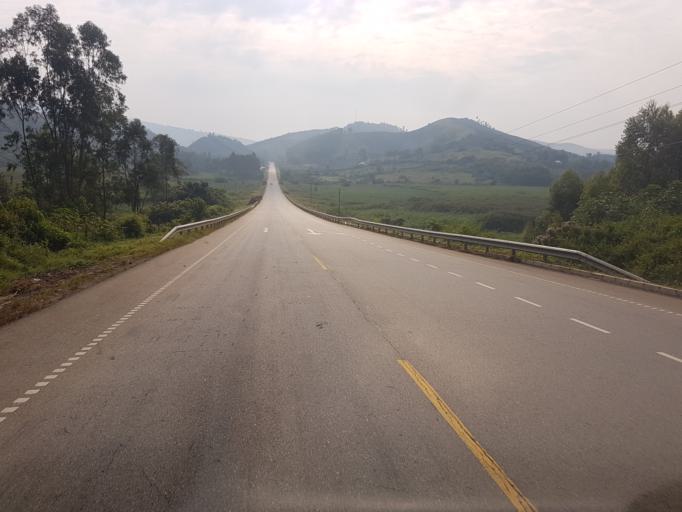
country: UG
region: Western Region
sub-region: Ntungamo District
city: Ntungamo
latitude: -0.7721
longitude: 30.2941
